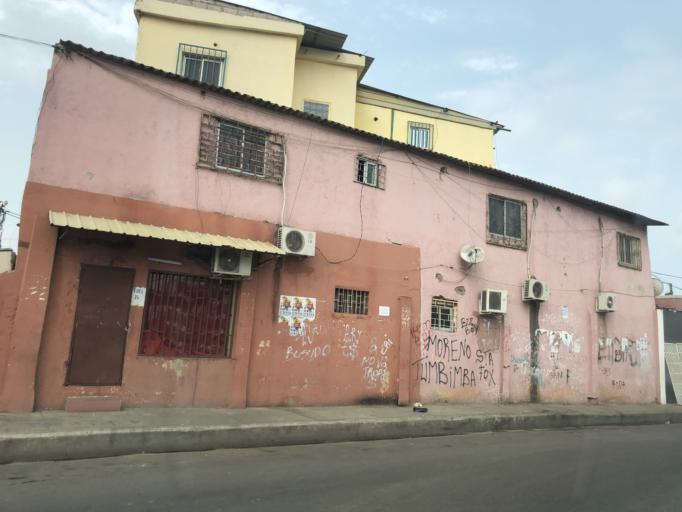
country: AO
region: Luanda
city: Luanda
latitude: -8.8398
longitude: 13.2357
